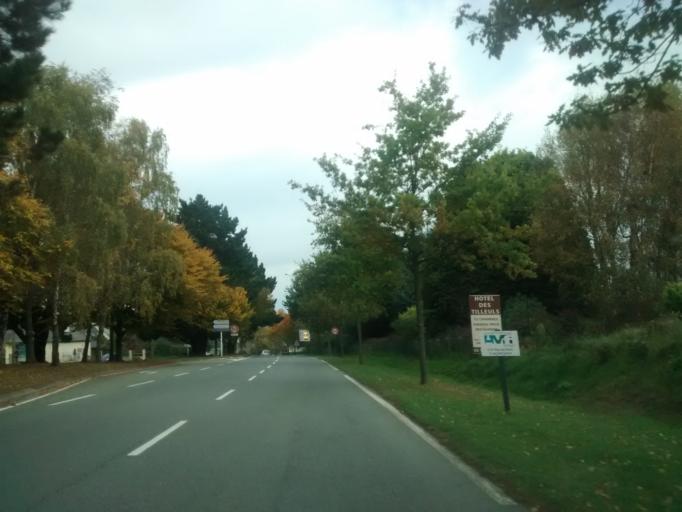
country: FR
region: Brittany
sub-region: Departement d'Ille-et-Vilaine
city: Dinard
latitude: 48.6171
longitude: -2.0575
